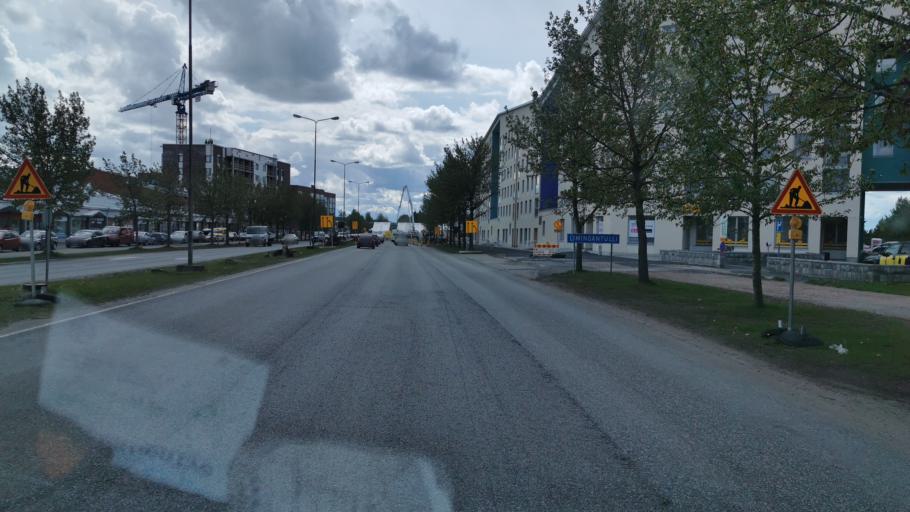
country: FI
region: Northern Ostrobothnia
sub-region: Oulu
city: Oulu
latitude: 65.0029
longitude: 25.4633
